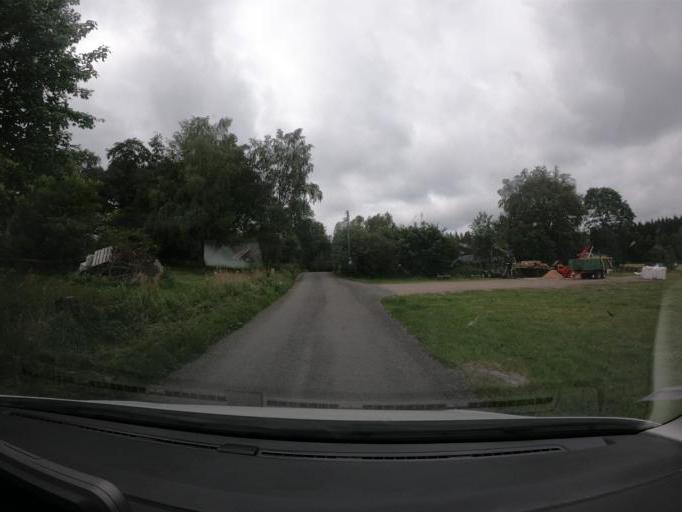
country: SE
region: Skane
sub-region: Perstorps Kommun
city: Perstorp
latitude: 56.1723
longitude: 13.5033
